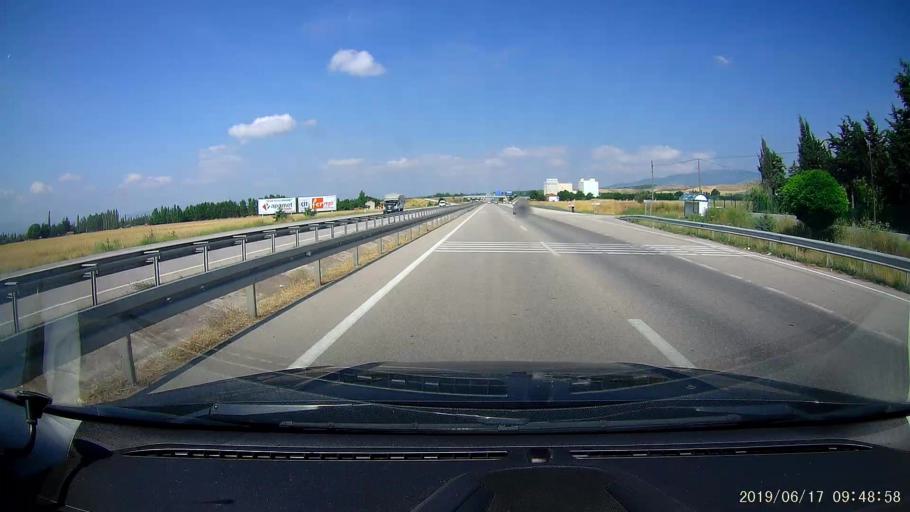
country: TR
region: Amasya
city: Merzifon
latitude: 40.8730
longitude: 35.5396
